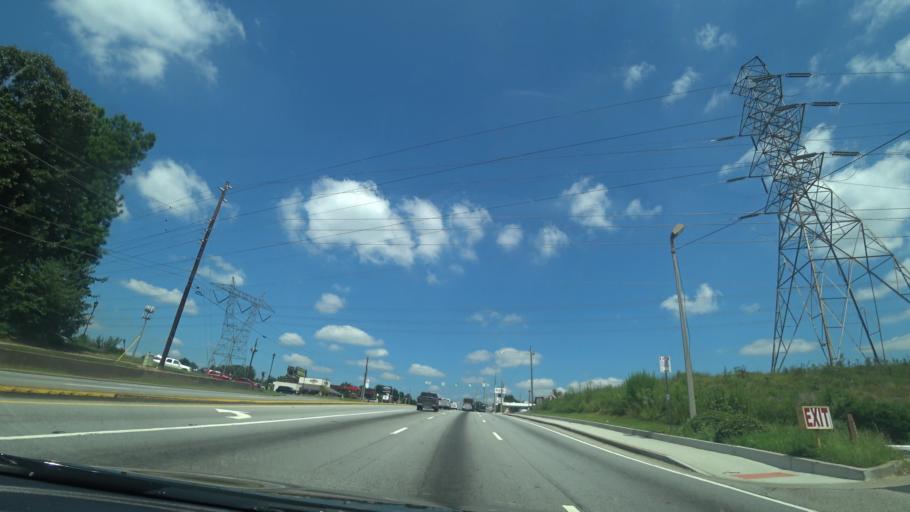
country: US
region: Georgia
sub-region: Gwinnett County
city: Norcross
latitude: 33.9306
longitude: -84.2213
